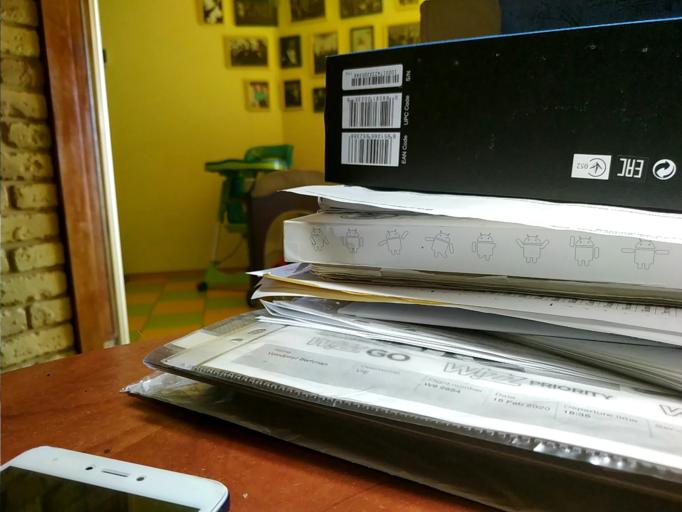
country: RU
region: Novgorod
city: Kholm
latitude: 59.2451
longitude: 32.8725
